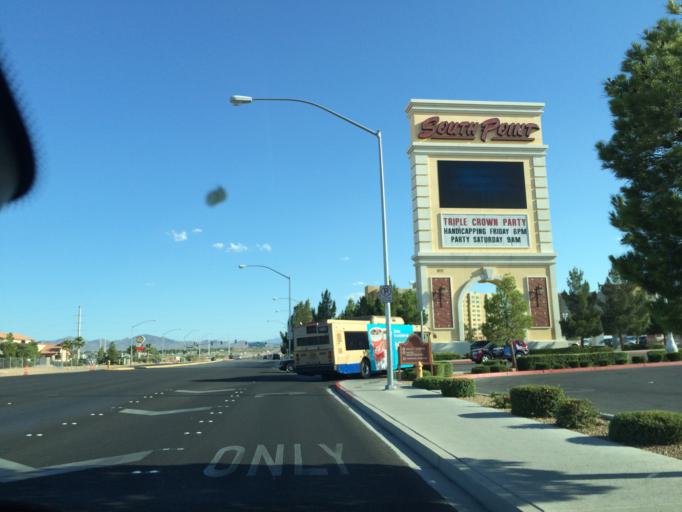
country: US
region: Nevada
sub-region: Clark County
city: Enterprise
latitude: 36.0124
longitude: -115.1726
